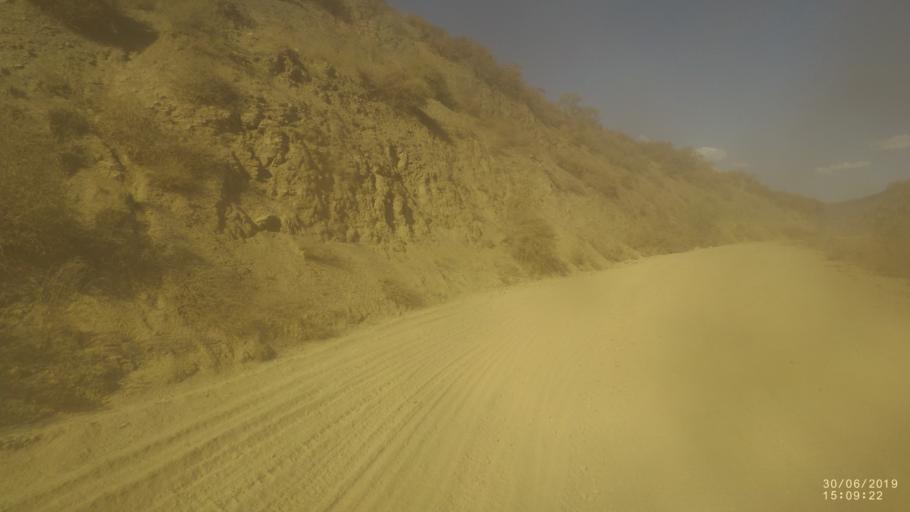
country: BO
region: Cochabamba
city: Irpa Irpa
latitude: -17.7289
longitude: -66.2994
